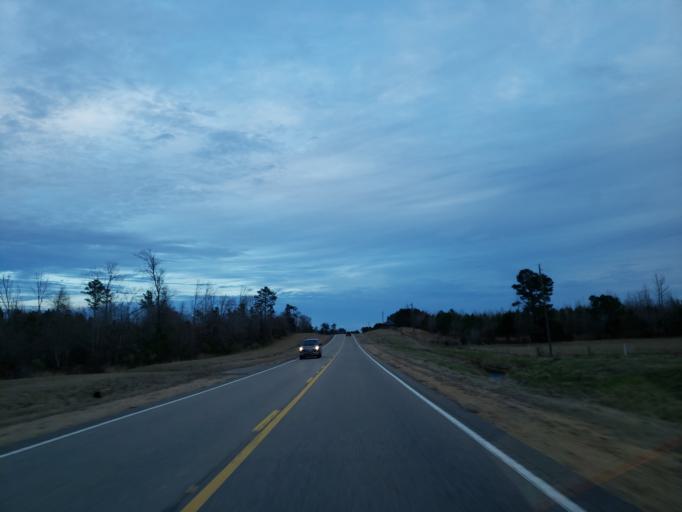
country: US
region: Mississippi
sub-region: Kemper County
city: De Kalb
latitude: 32.8308
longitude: -88.3750
